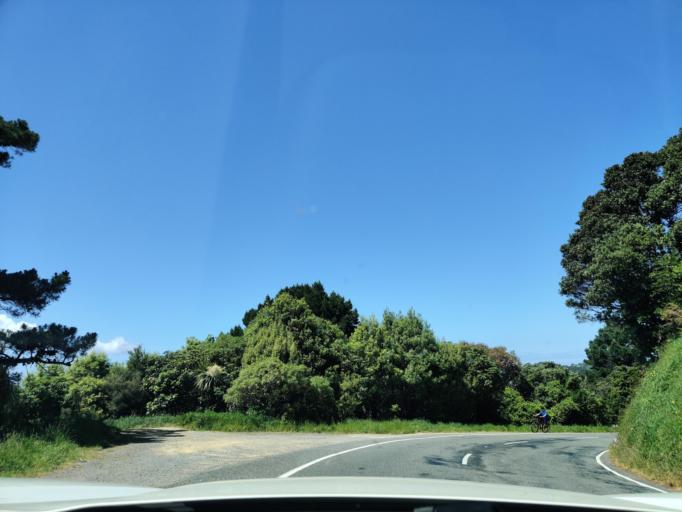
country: NZ
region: Wellington
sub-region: Wellington City
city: Wellington
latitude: -41.3031
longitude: 174.7892
